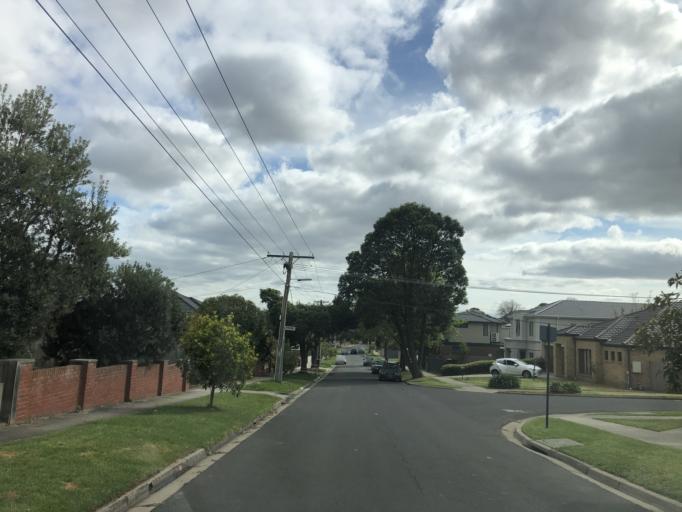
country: AU
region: Victoria
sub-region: Monash
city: Chadstone
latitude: -37.8804
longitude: 145.0960
